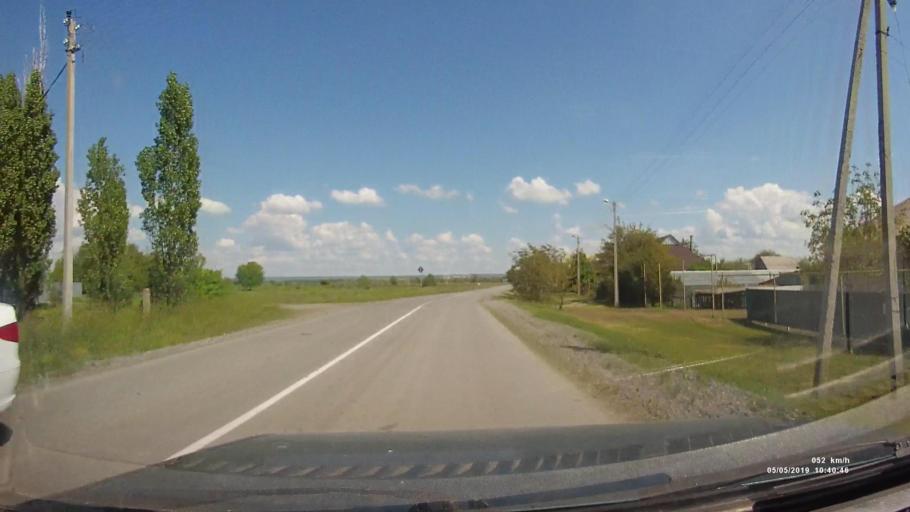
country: RU
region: Rostov
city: Ust'-Donetskiy
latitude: 47.5866
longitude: 40.8421
